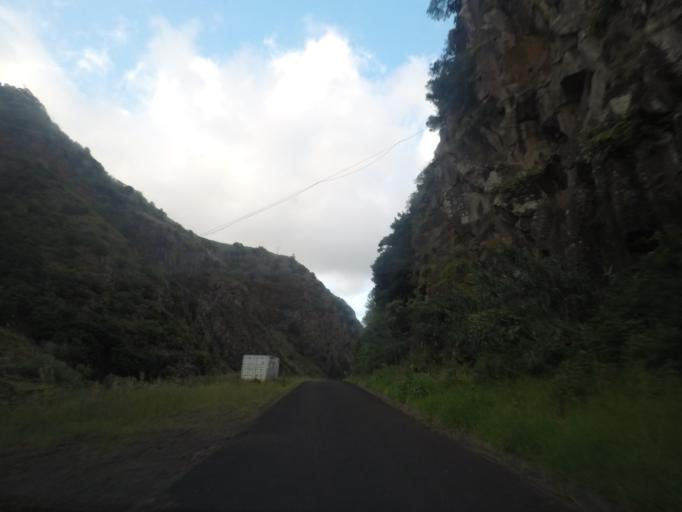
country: PT
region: Madeira
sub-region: Porto Moniz
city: Porto Moniz
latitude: 32.8508
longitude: -17.1597
